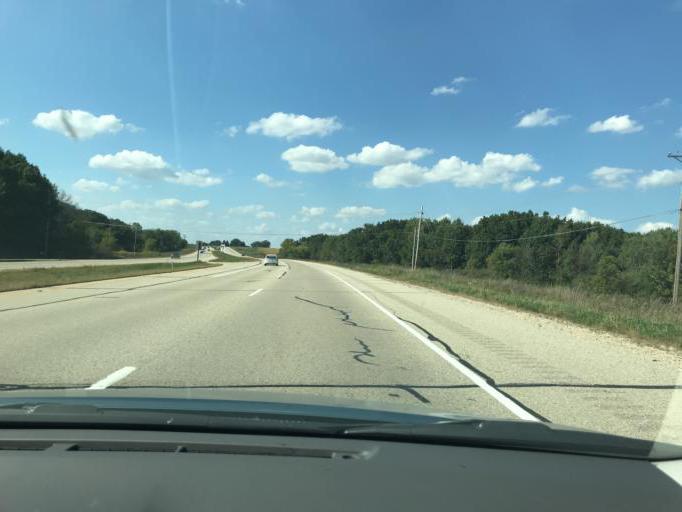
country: US
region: Wisconsin
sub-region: Walworth County
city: Pell Lake
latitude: 42.5893
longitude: -88.3416
